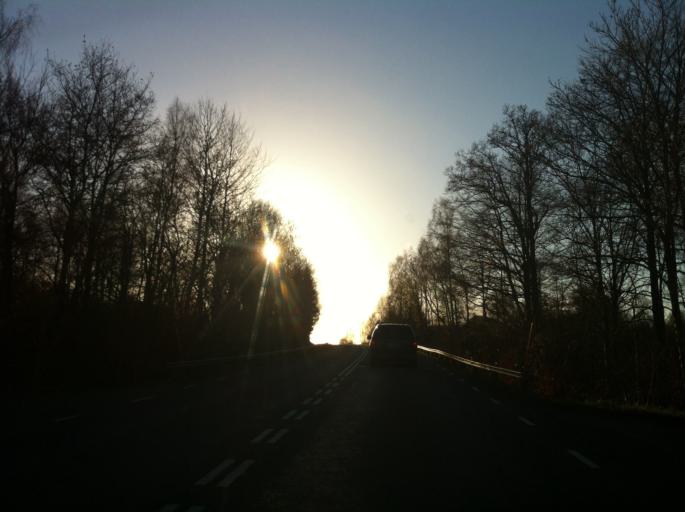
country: SE
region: Skane
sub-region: Bromolla Kommun
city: Nasum
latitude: 56.1756
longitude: 14.3873
